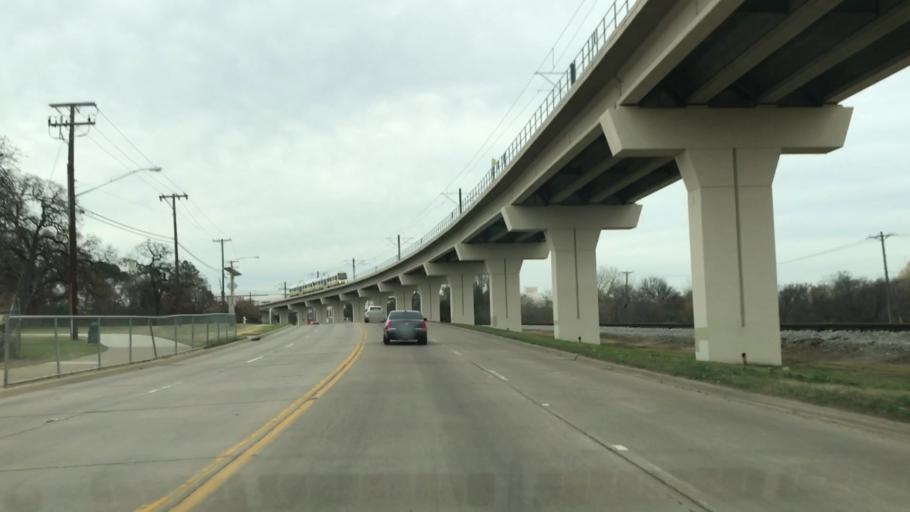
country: US
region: Texas
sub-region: Dallas County
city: University Park
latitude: 32.8473
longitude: -96.8720
